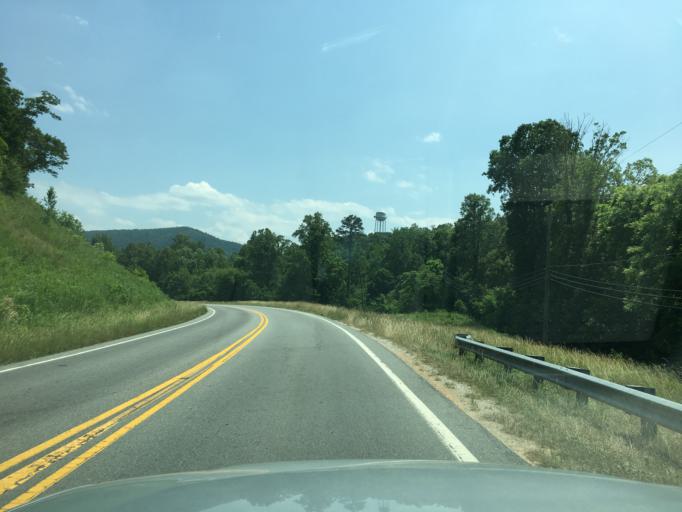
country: US
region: North Carolina
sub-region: McDowell County
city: Marion
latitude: 35.6491
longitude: -81.9550
